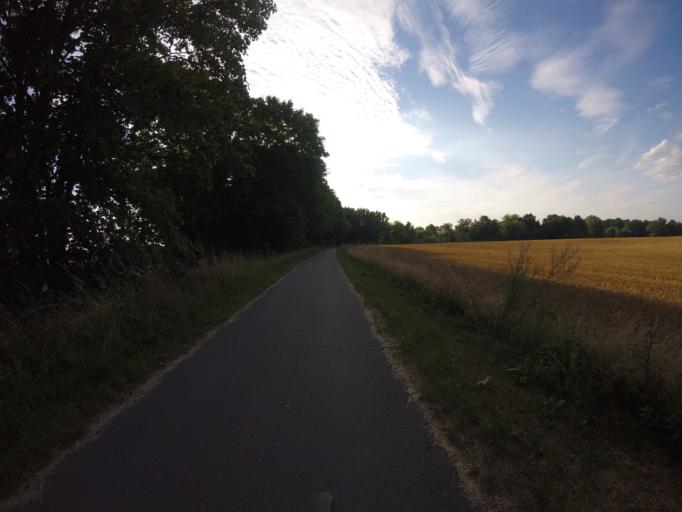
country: DE
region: Brandenburg
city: Altlandsberg
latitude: 52.5623
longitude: 13.7577
